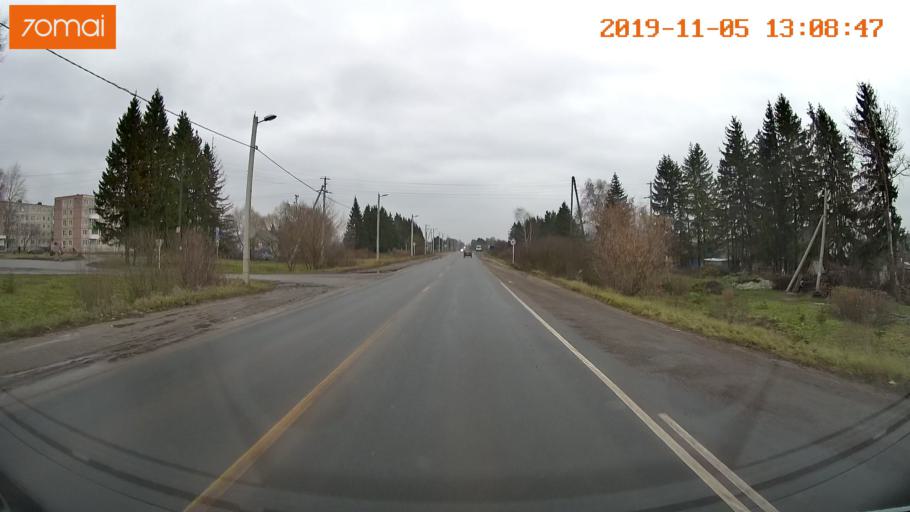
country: RU
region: Ivanovo
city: Kitovo
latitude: 56.8636
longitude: 41.2971
